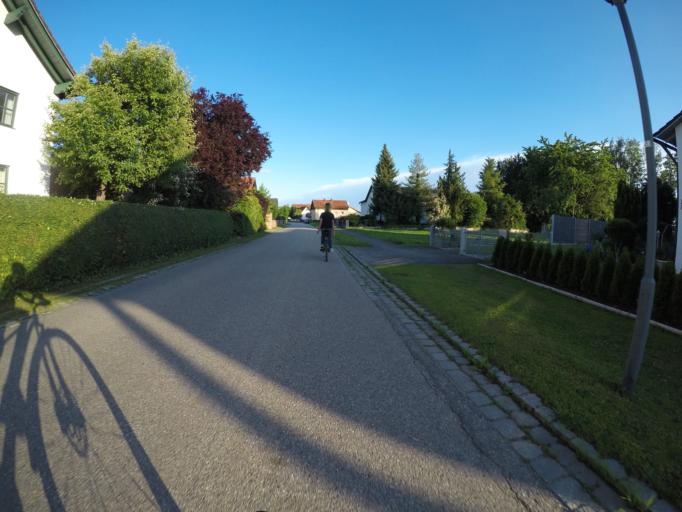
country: DE
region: Bavaria
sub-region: Lower Bavaria
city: Reisbach
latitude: 48.5784
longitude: 12.6233
